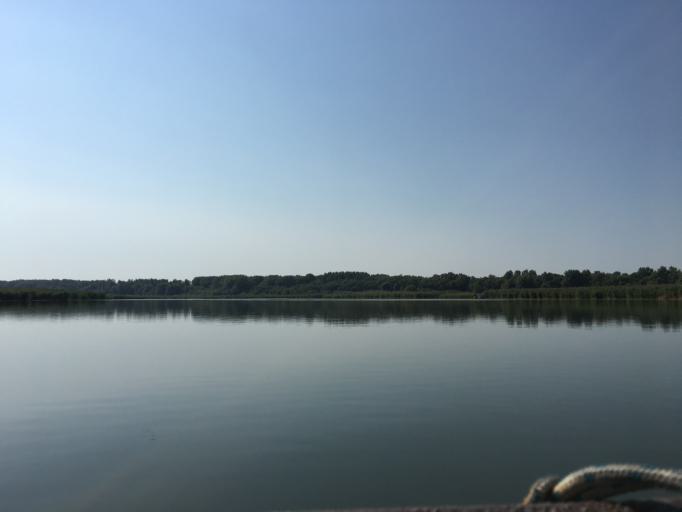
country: HU
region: Jasz-Nagykun-Szolnok
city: Tiszafured
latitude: 47.6538
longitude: 20.7324
